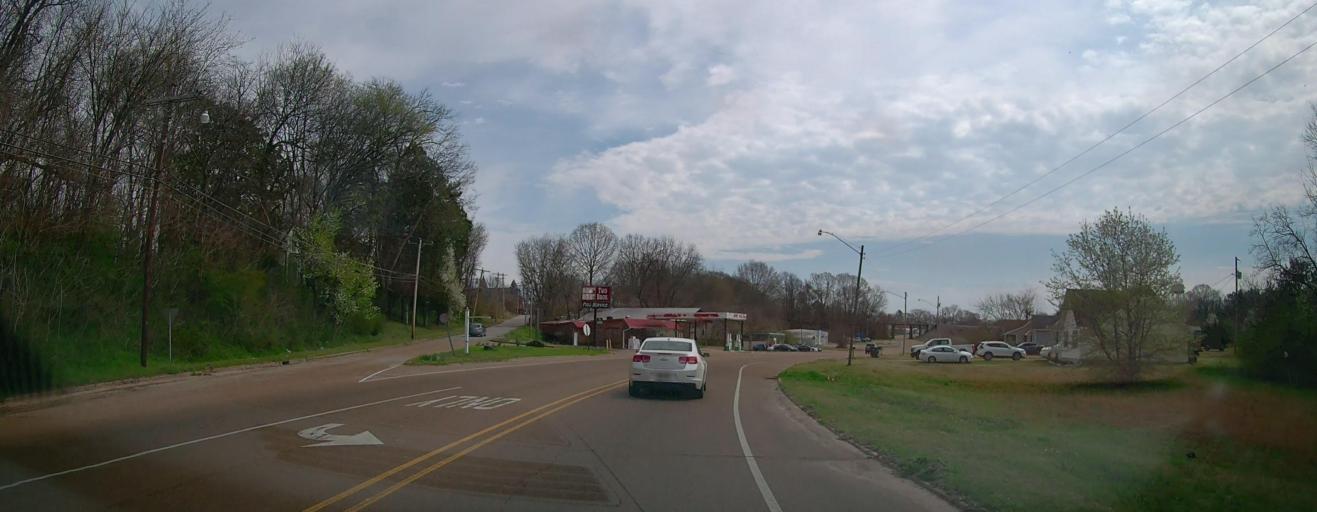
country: US
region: Mississippi
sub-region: Marshall County
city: Holly Springs
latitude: 34.7675
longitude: -89.4375
